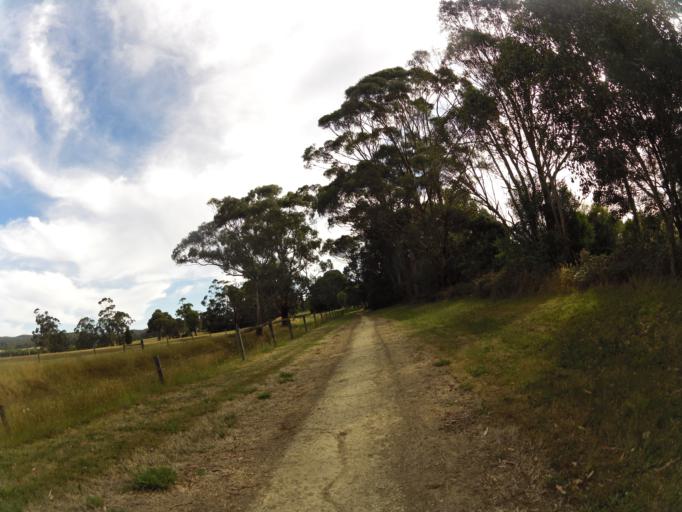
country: AU
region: Victoria
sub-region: Colac-Otway
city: Colac
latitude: -38.5101
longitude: 143.7177
